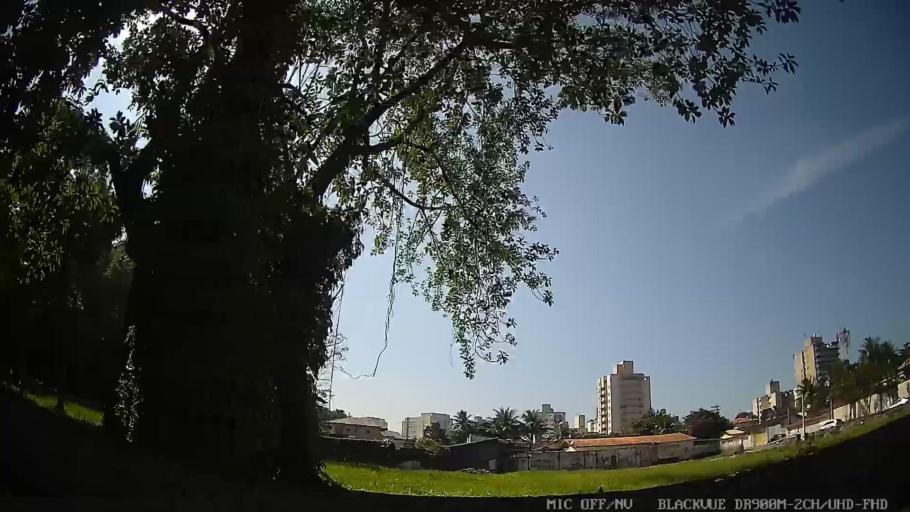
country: BR
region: Sao Paulo
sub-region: Guaruja
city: Guaruja
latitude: -24.0115
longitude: -46.2796
